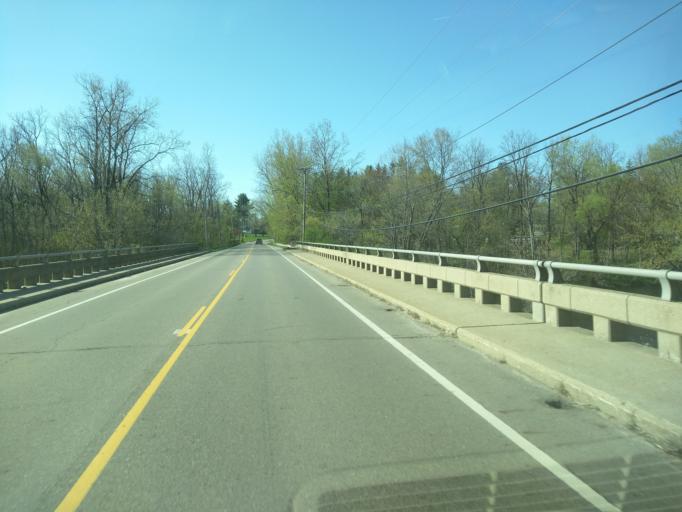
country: US
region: Michigan
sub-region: Eaton County
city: Waverly
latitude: 42.7611
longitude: -84.6488
